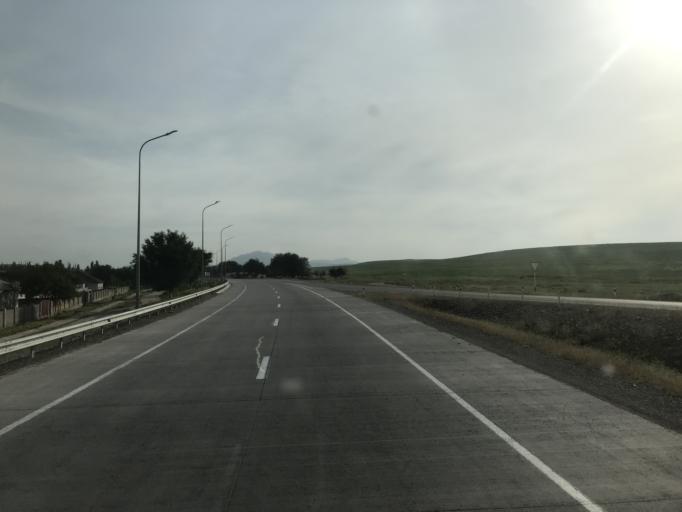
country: KZ
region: Ongtustik Qazaqstan
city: Qazyqurt
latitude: 41.9013
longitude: 69.4608
